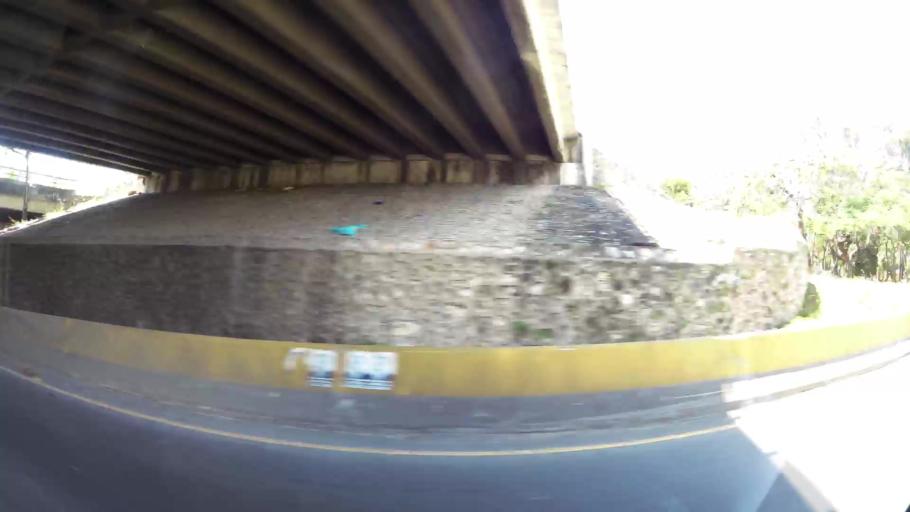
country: DO
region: Santo Domingo
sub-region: Santo Domingo
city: Santo Domingo Este
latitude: 18.4850
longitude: -69.8488
